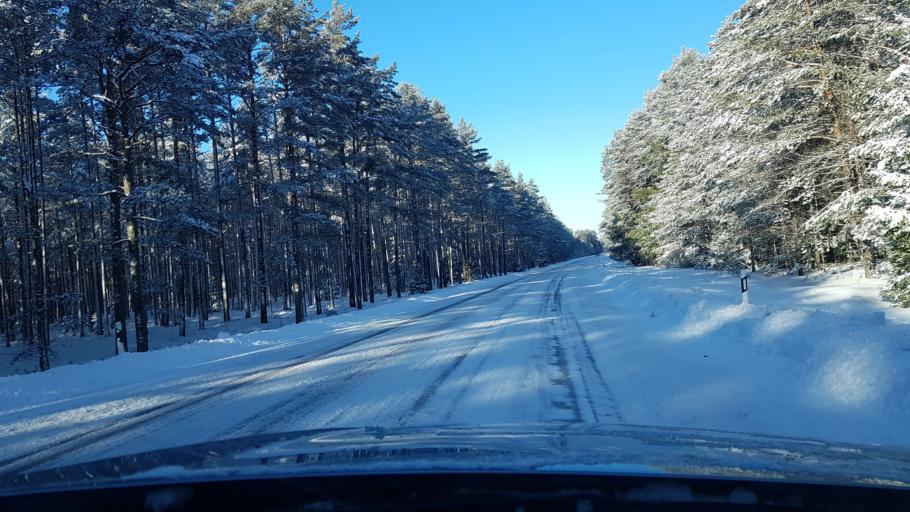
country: EE
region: Hiiumaa
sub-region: Kaerdla linn
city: Kardla
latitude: 58.9288
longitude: 22.7846
